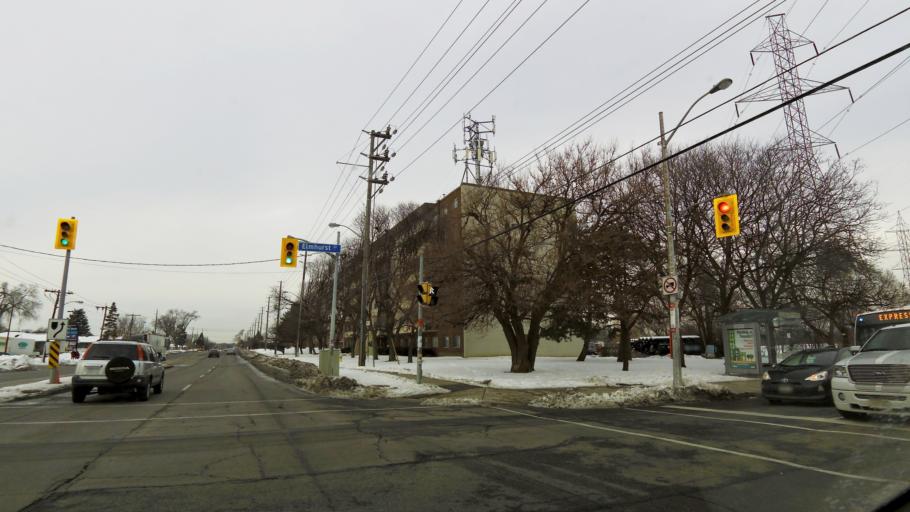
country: CA
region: Ontario
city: Etobicoke
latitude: 43.7230
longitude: -79.5587
